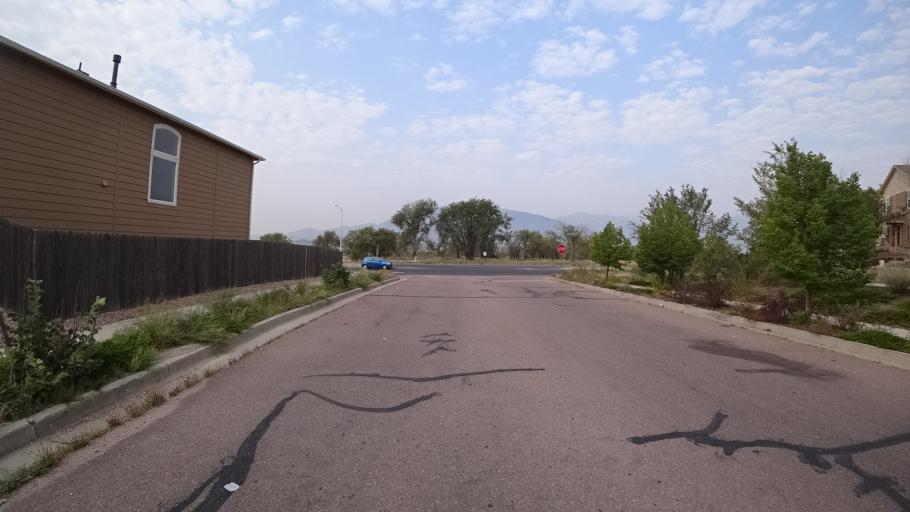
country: US
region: Colorado
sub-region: El Paso County
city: Stratmoor
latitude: 38.7992
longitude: -104.7773
